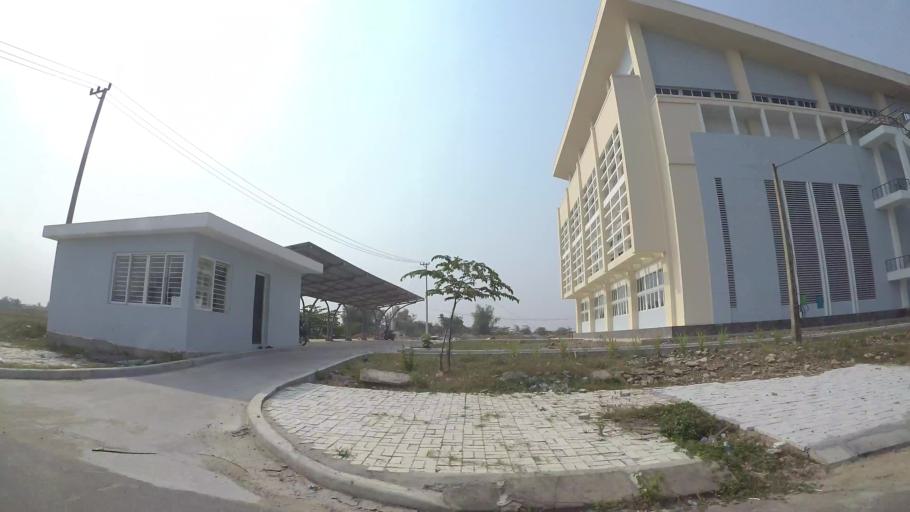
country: VN
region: Da Nang
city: Cam Le
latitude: 15.9983
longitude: 108.2190
